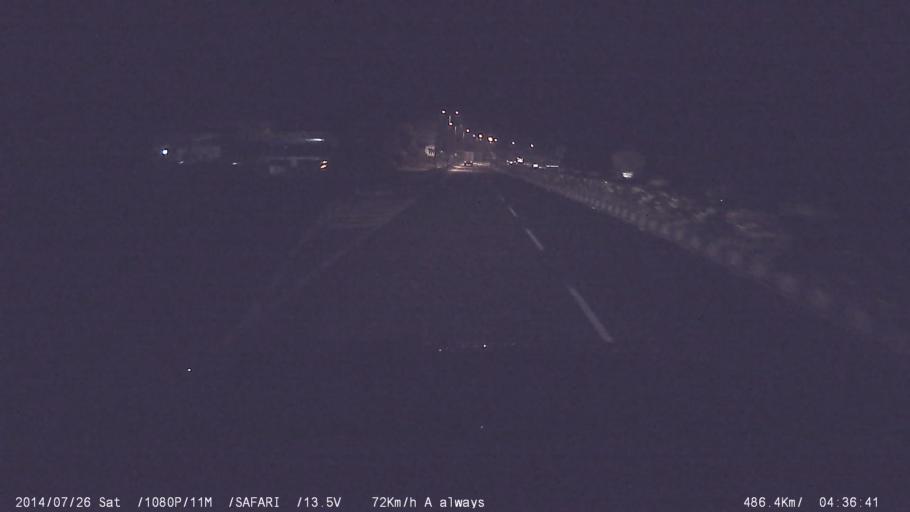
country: IN
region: Kerala
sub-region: Thrissur District
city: Kizhake Chalakudi
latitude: 10.2594
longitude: 76.3621
